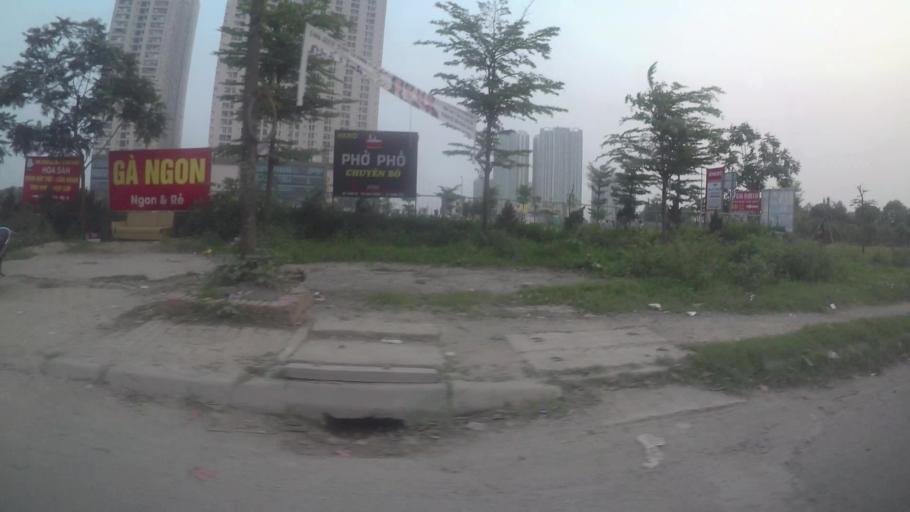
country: VN
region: Ha Noi
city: Cau Dien
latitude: 21.0101
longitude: 105.7296
